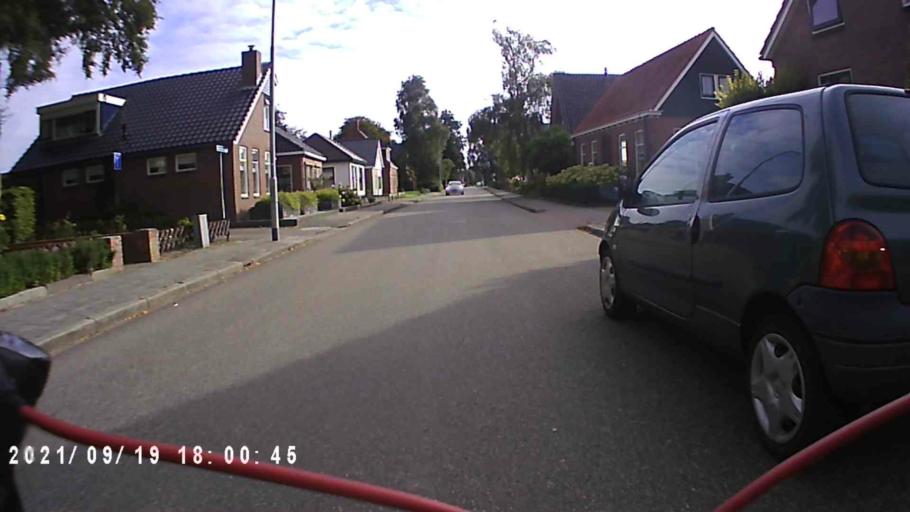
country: NL
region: Groningen
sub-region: Gemeente Delfzijl
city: Delfzijl
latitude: 53.2553
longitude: 6.9299
